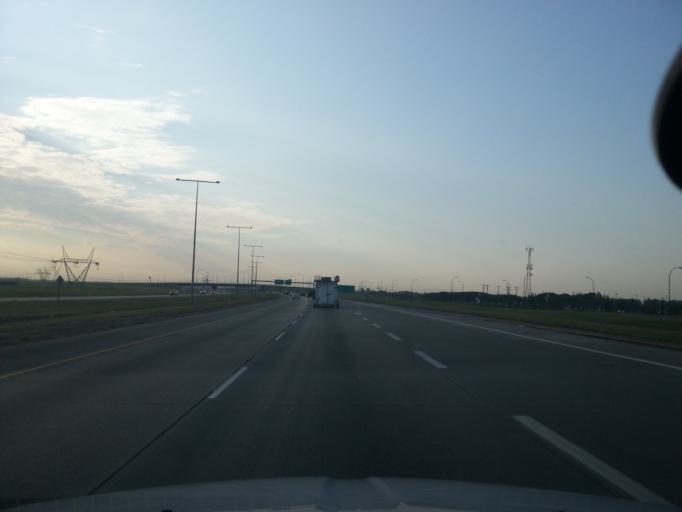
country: CA
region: Alberta
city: Devon
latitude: 53.4350
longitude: -113.5924
